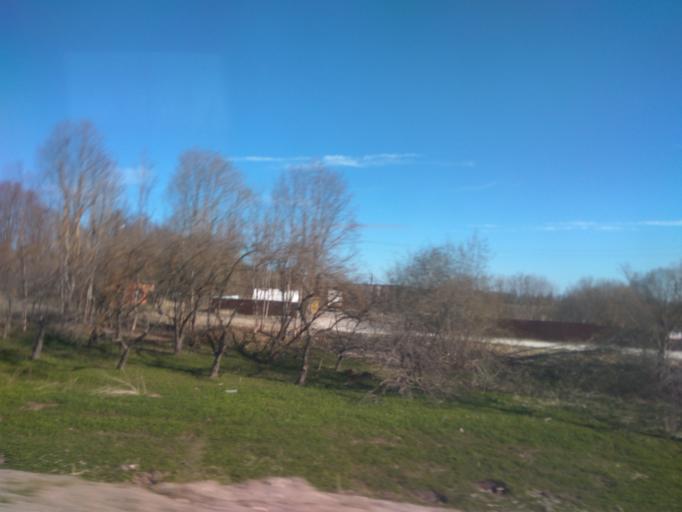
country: RU
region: Pskov
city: Izborsk
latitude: 57.7045
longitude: 27.8517
